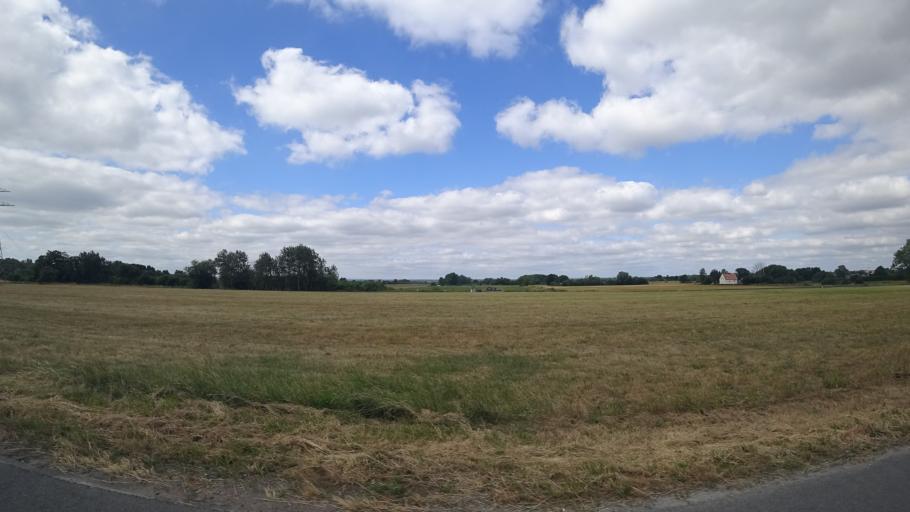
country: SE
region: Skane
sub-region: Kristianstads Kommun
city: Fjalkinge
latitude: 55.9992
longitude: 14.2680
